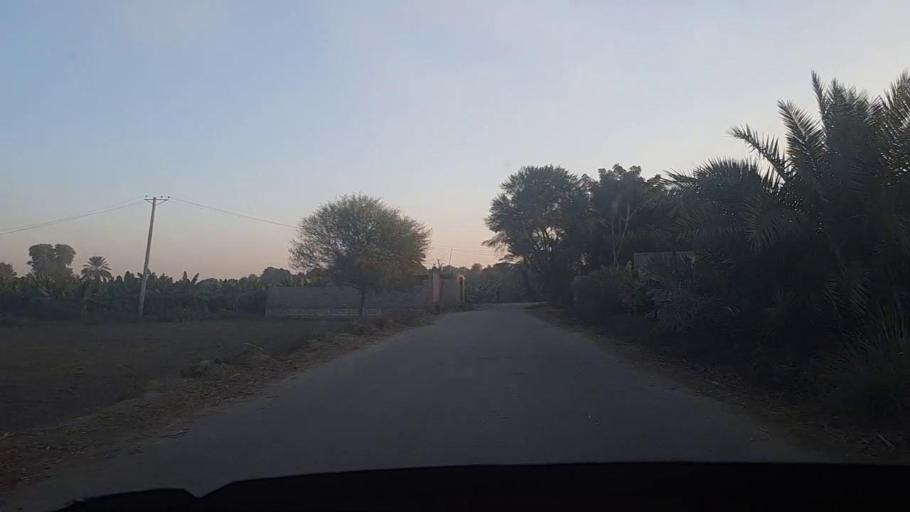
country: PK
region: Sindh
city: Sobhadero
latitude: 27.3398
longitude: 68.3788
